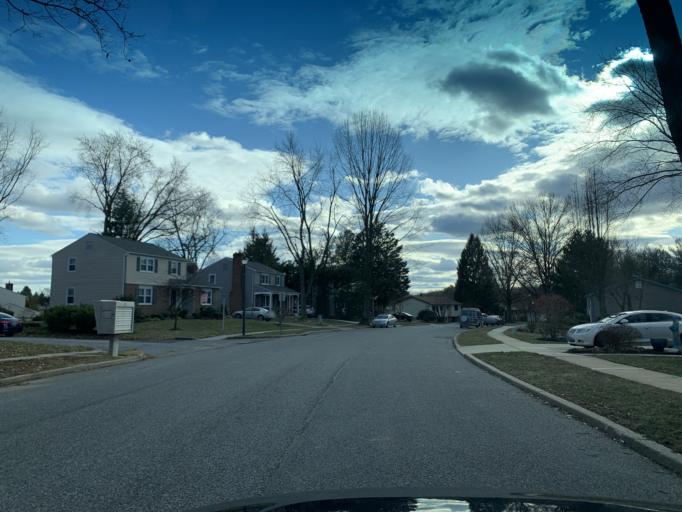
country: US
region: Maryland
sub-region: Harford County
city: South Bel Air
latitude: 39.5307
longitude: -76.3253
